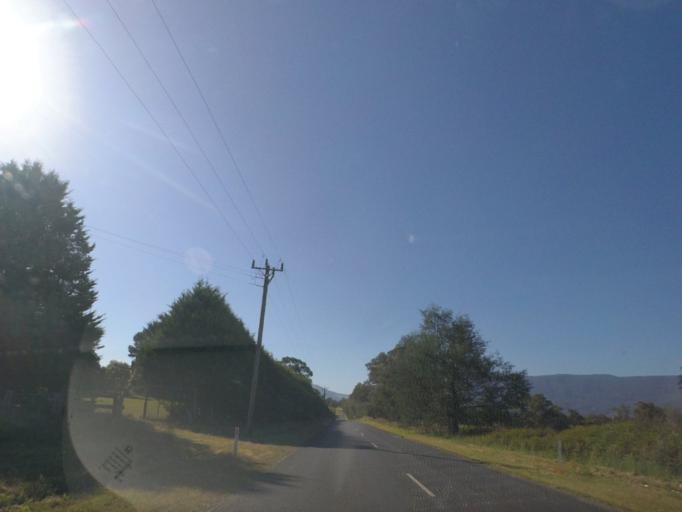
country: AU
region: Victoria
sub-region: Yarra Ranges
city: Yarra Junction
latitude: -37.8024
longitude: 145.6347
